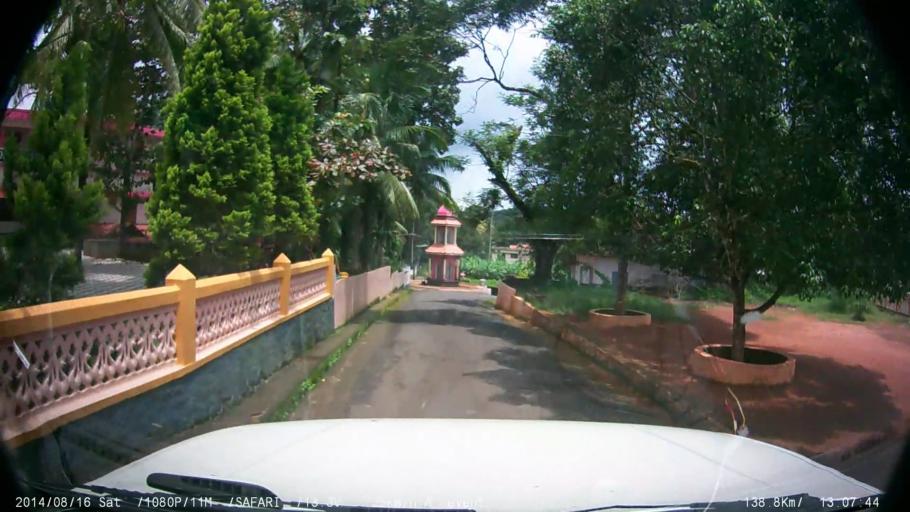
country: IN
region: Kerala
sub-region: Kottayam
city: Palackattumala
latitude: 9.7807
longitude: 76.5773
